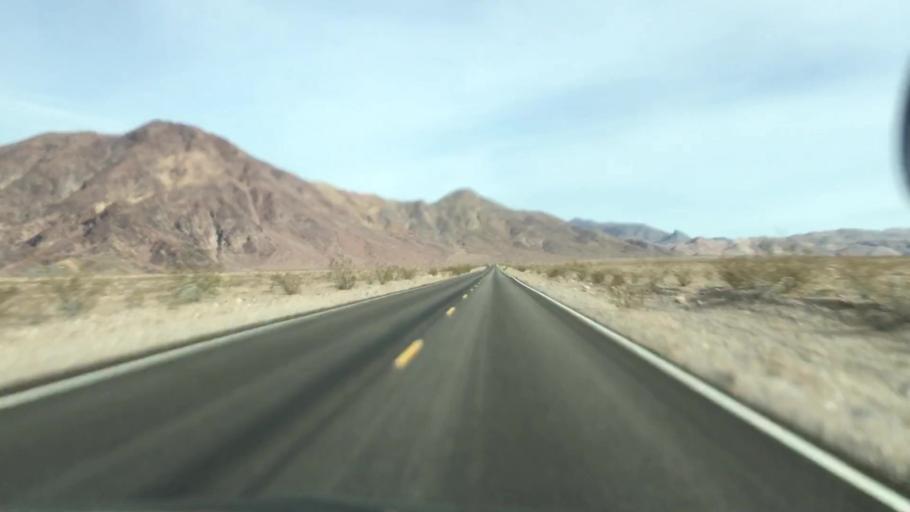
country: US
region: Nevada
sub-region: Nye County
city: Beatty
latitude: 36.6870
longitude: -117.0050
